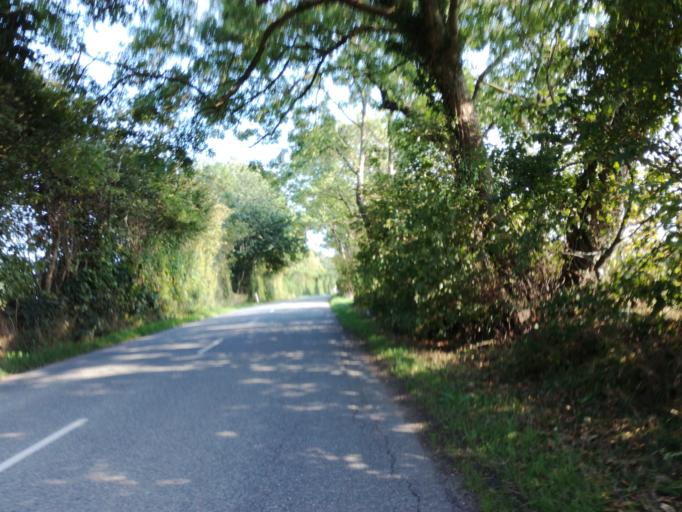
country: DK
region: South Denmark
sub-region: Vejle Kommune
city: Borkop
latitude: 55.6504
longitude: 9.6579
